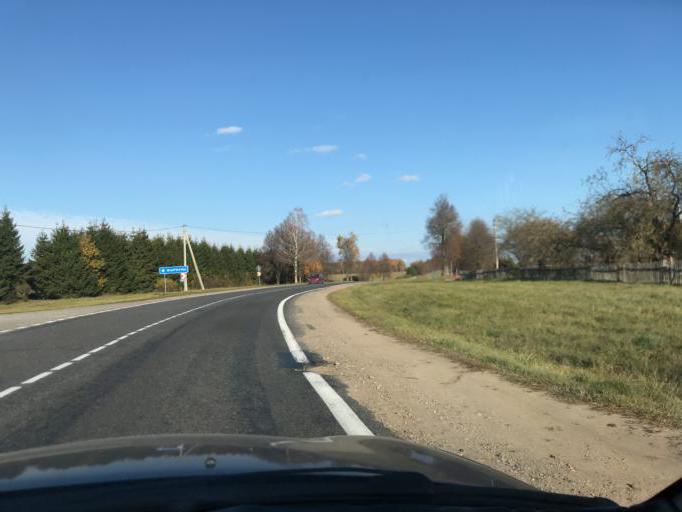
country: BY
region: Grodnenskaya
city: Lida
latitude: 53.9958
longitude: 25.2122
